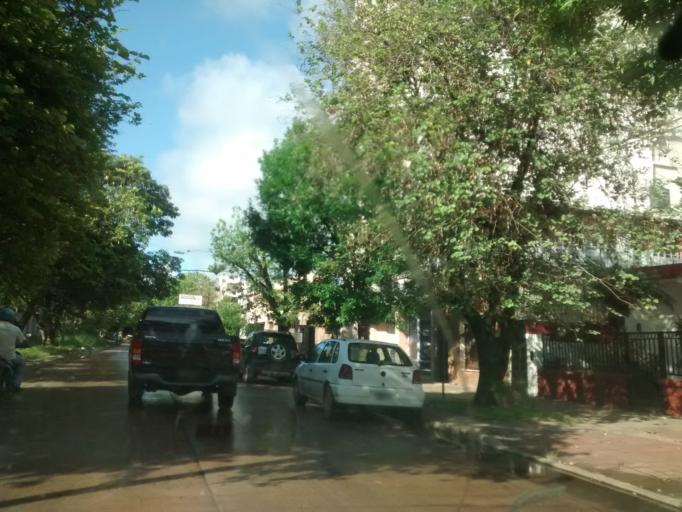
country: AR
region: Chaco
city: Resistencia
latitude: -27.4590
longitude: -58.9883
